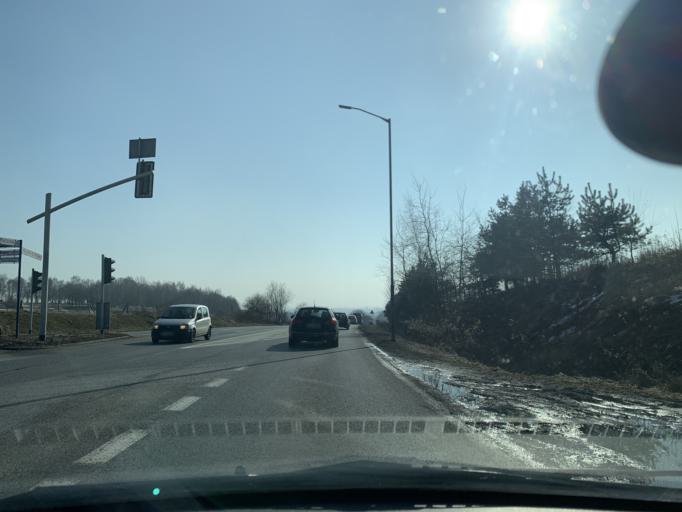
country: PL
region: Silesian Voivodeship
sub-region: Piekary Slaskie
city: Piekary Slaskie
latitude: 50.3938
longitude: 18.9272
